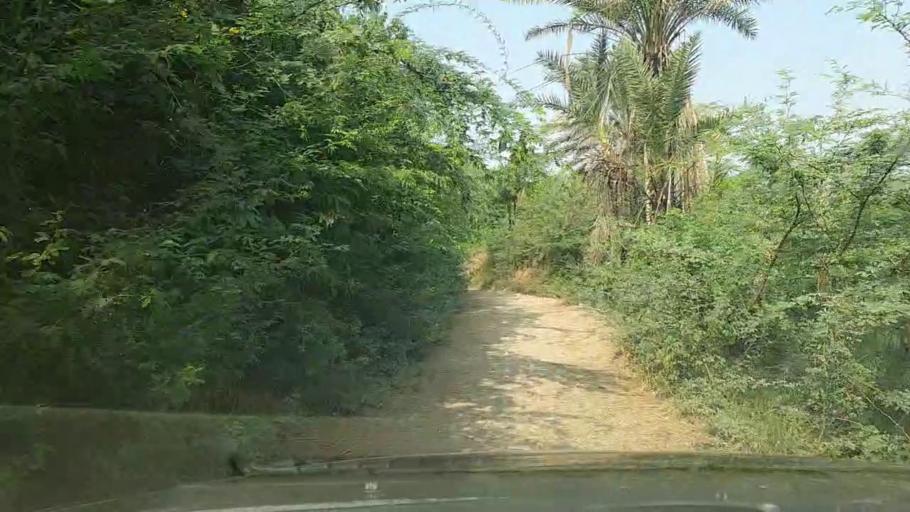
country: PK
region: Sindh
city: Mirpur Batoro
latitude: 24.6824
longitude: 68.2369
